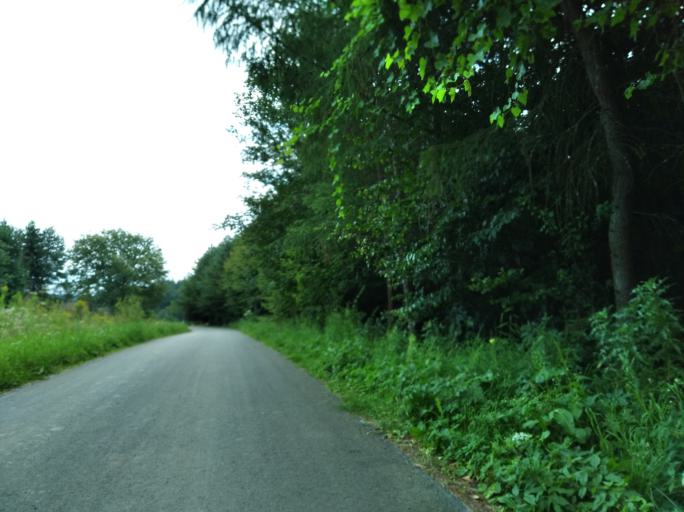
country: PL
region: Subcarpathian Voivodeship
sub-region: Powiat krosnienski
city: Wojaszowka
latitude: 49.7816
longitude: 21.7067
